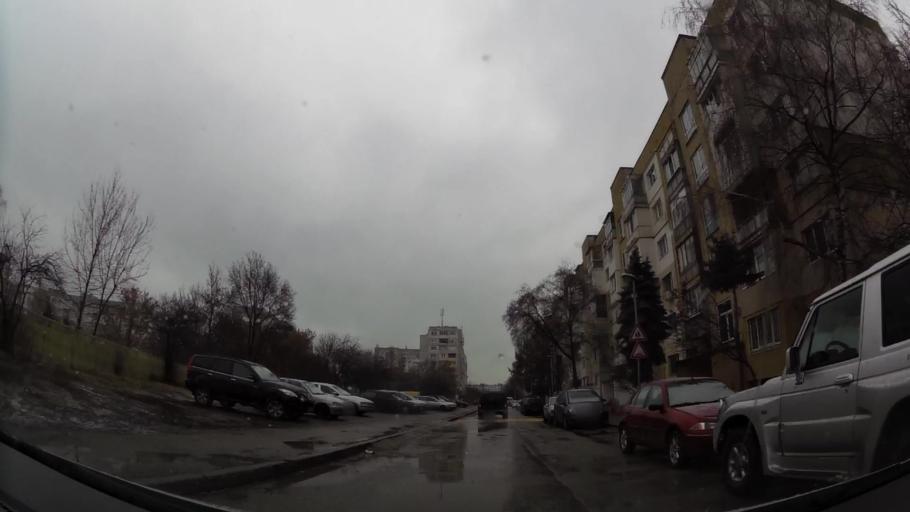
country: BG
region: Sofia-Capital
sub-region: Stolichna Obshtina
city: Sofia
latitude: 42.6681
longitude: 23.3876
